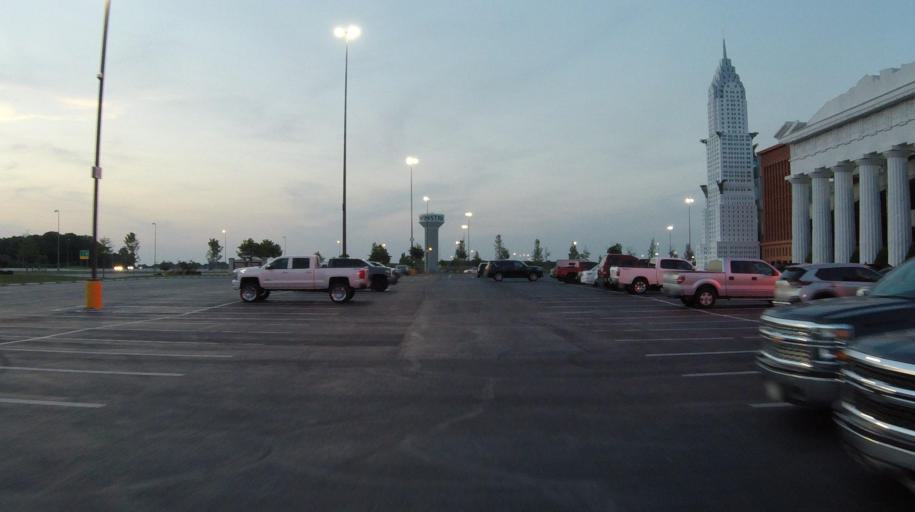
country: US
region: Texas
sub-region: Cooke County
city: Gainesville
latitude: 33.7590
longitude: -97.1336
